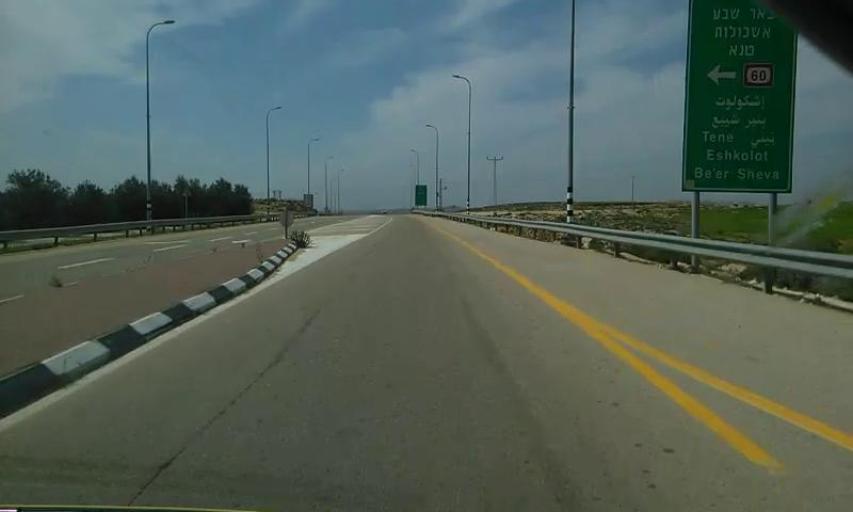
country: PS
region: West Bank
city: Az Zahiriyah
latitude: 31.3763
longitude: 35.0061
